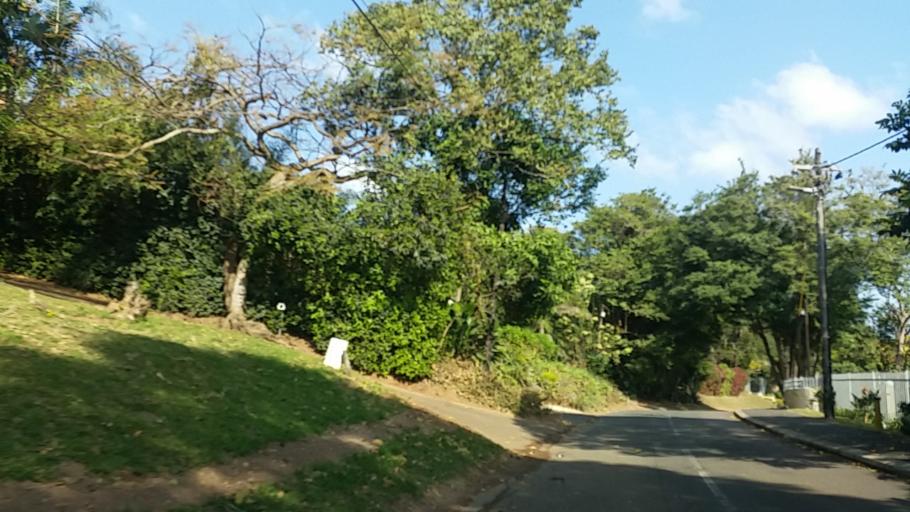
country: ZA
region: KwaZulu-Natal
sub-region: eThekwini Metropolitan Municipality
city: Berea
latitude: -29.8345
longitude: 30.9069
